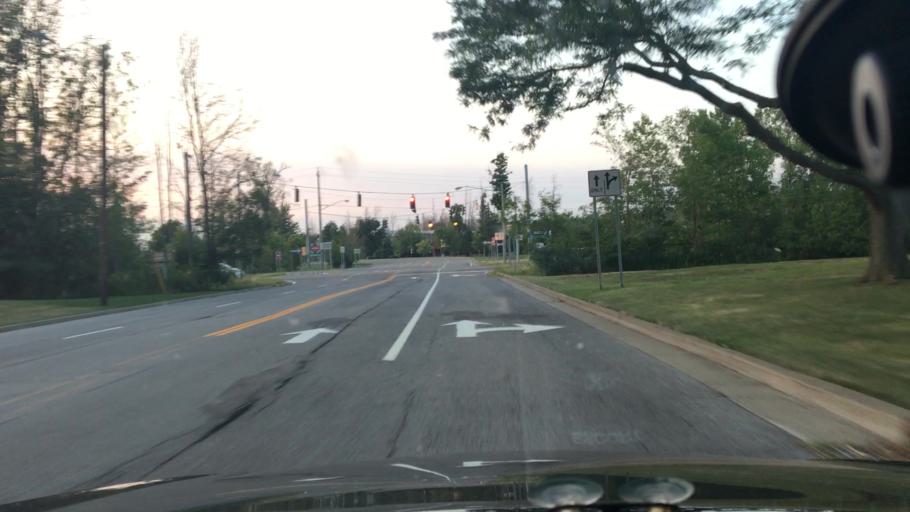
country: US
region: New York
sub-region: Erie County
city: Orchard Park
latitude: 42.7881
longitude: -78.7664
